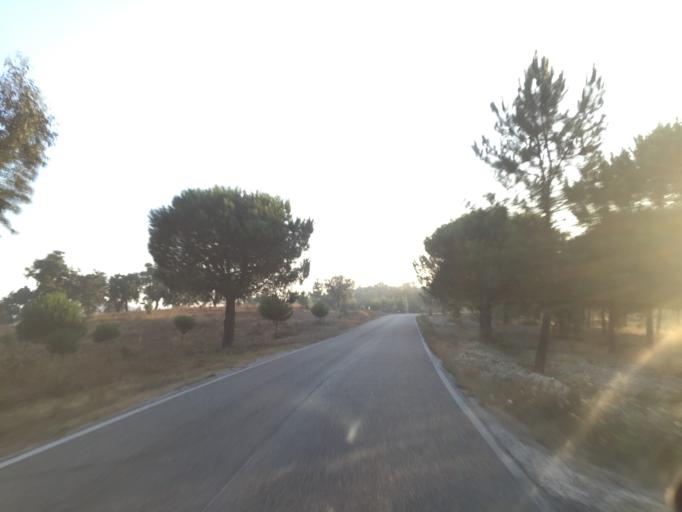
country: PT
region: Santarem
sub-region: Coruche
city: Coruche
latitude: 39.0406
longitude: -8.4407
